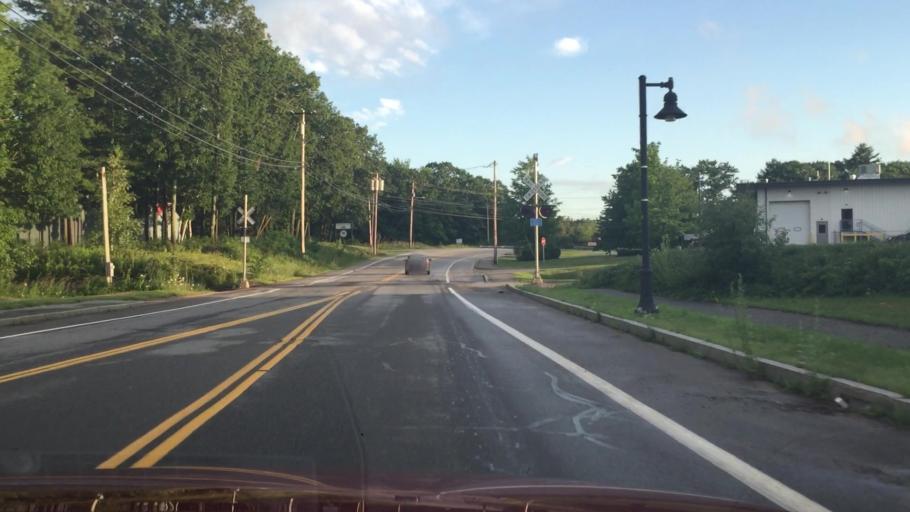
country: US
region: Maine
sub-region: Cumberland County
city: South Portland Gardens
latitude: 43.6689
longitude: -70.3226
